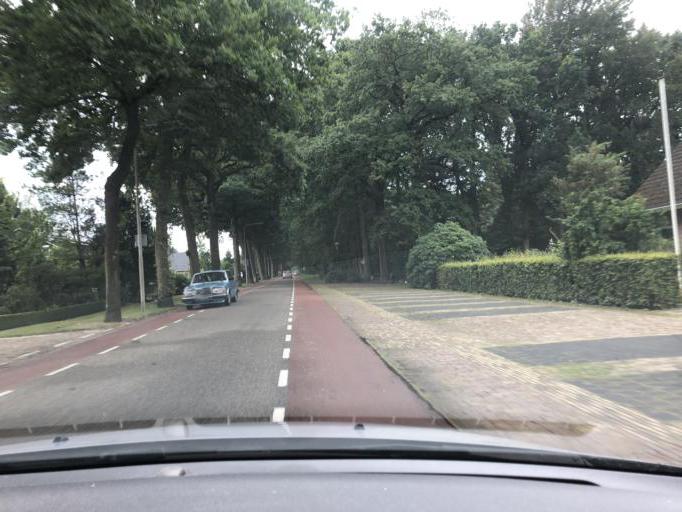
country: NL
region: Overijssel
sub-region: Gemeente Dalfsen
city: Dalfsen
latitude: 52.5722
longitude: 6.2930
